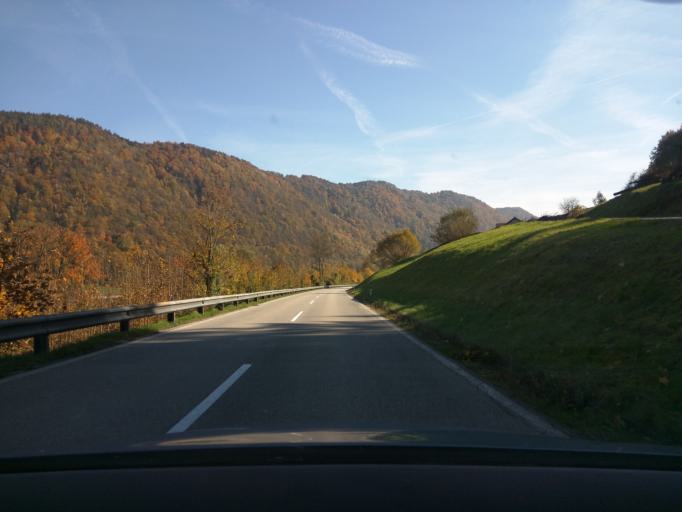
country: DE
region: Bavaria
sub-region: Lower Bavaria
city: Untergriesbach
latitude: 48.5134
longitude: 13.7199
